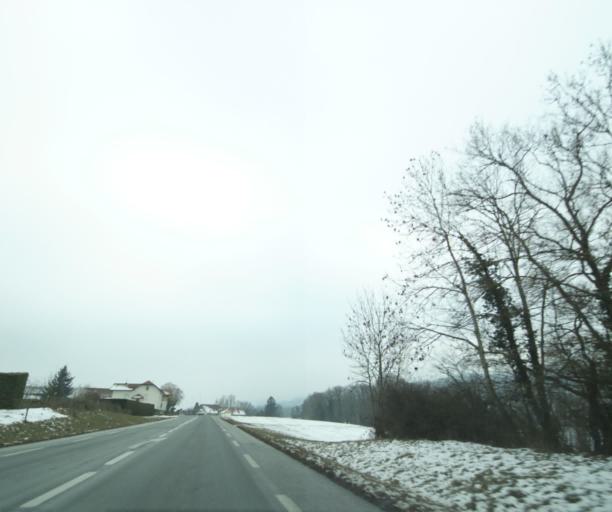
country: FR
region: Rhone-Alpes
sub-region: Departement de la Haute-Savoie
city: Pers-Jussy
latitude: 46.1167
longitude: 6.2721
